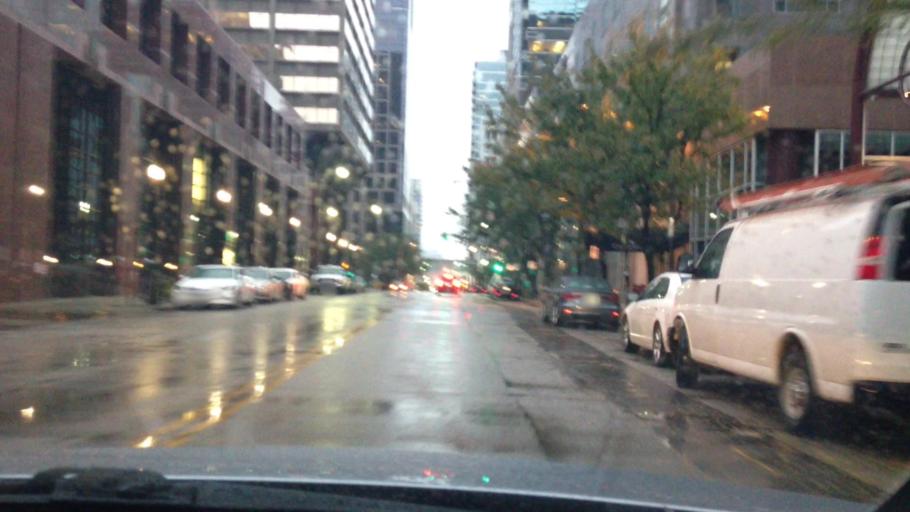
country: US
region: Missouri
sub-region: Jackson County
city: Kansas City
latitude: 39.1021
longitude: -94.5820
